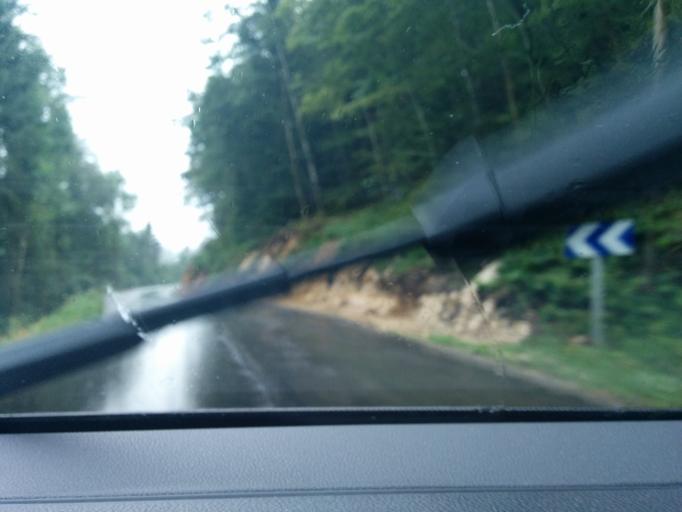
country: FR
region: Franche-Comte
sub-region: Departement du Jura
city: Valfin-les-Saint-Claude
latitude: 46.4674
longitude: 5.8350
